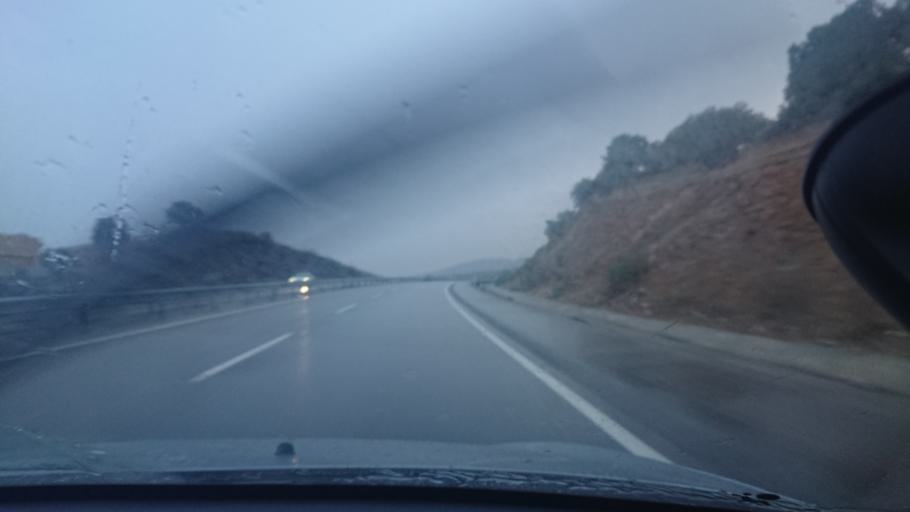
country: TR
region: Manisa
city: Menye
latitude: 38.5297
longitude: 28.4150
